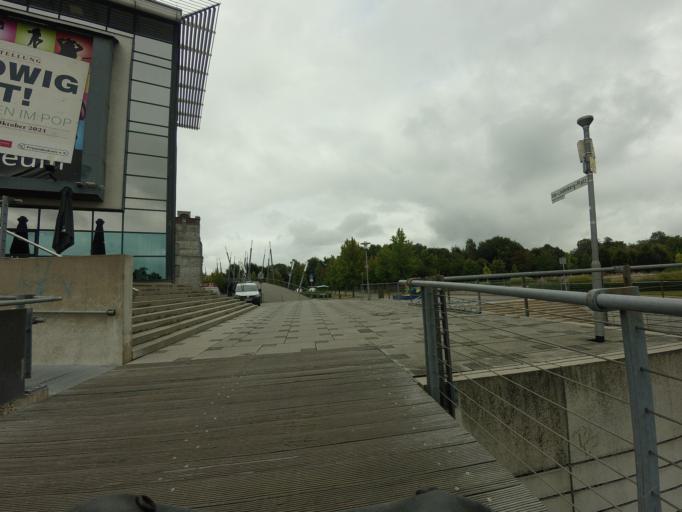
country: DE
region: North Rhine-Westphalia
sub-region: Regierungsbezirk Munster
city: Gronau
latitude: 52.2136
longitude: 7.0260
